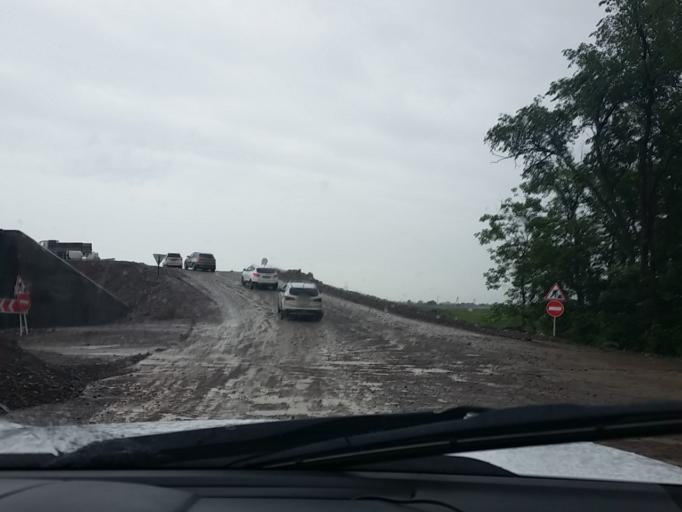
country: KZ
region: Almaty Oblysy
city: Turgen'
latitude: 43.5259
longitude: 77.5438
